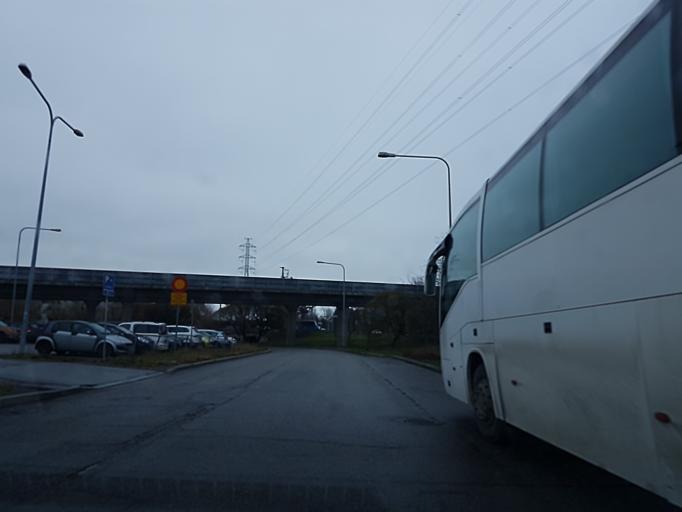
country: FI
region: Uusimaa
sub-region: Helsinki
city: Vantaa
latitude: 60.2388
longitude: 25.1074
